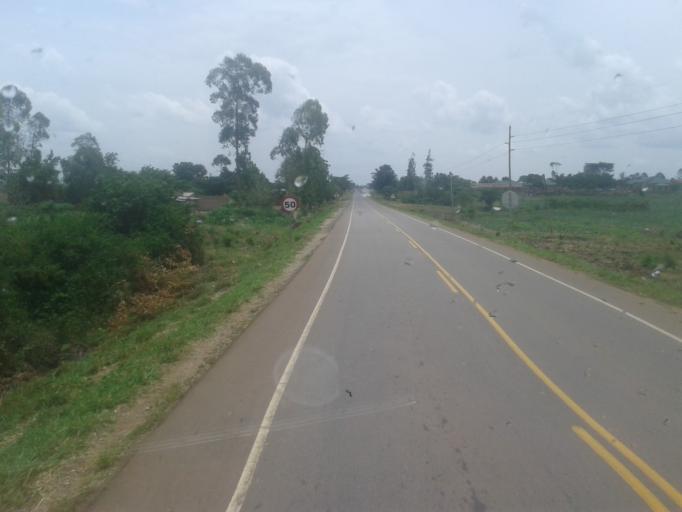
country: UG
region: Western Region
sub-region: Kiryandongo District
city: Kiryandongo
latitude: 1.7802
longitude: 32.0176
